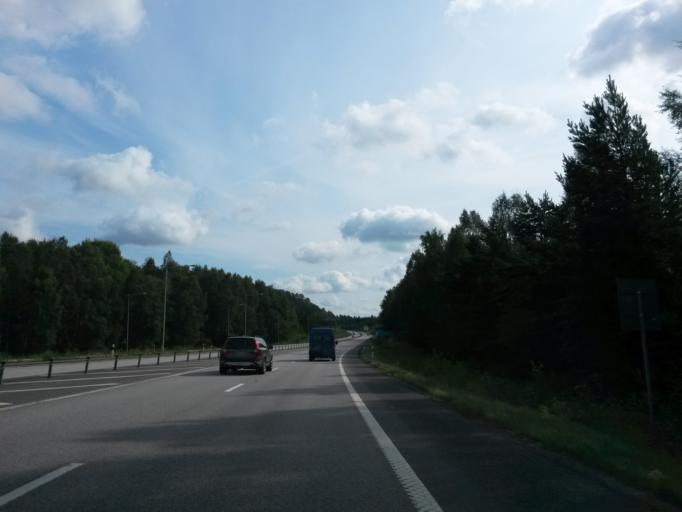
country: SE
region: Kronoberg
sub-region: Vaxjo Kommun
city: Vaexjoe
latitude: 56.8907
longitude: 14.7565
